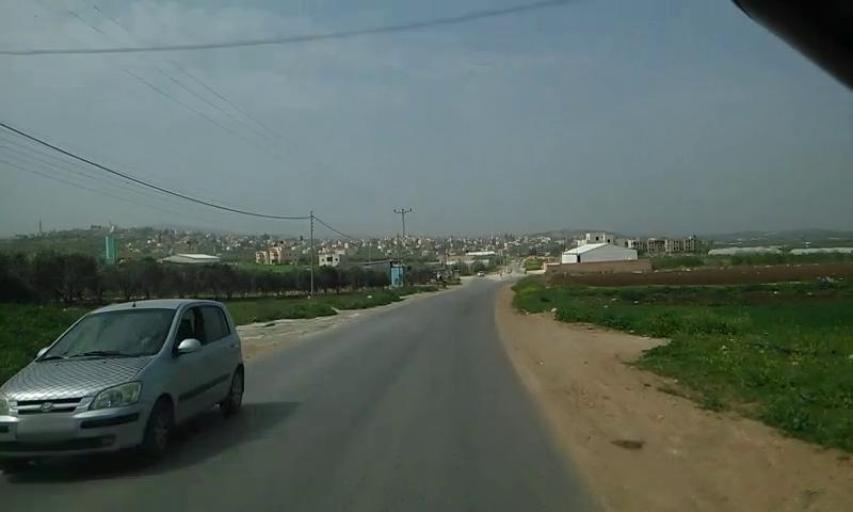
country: PS
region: West Bank
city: Silat al Harithiyah
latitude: 32.5021
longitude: 35.2441
